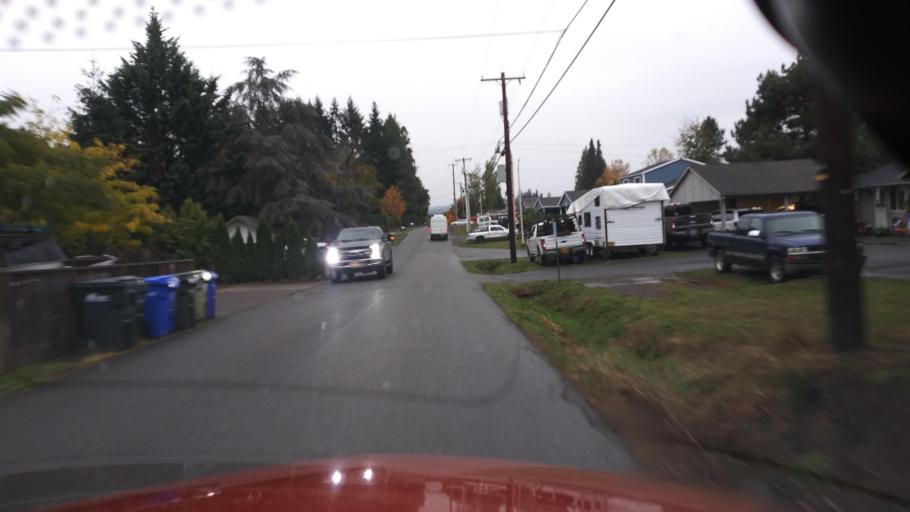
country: US
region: Oregon
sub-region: Washington County
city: Cornelius
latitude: 45.5234
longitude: -123.0358
